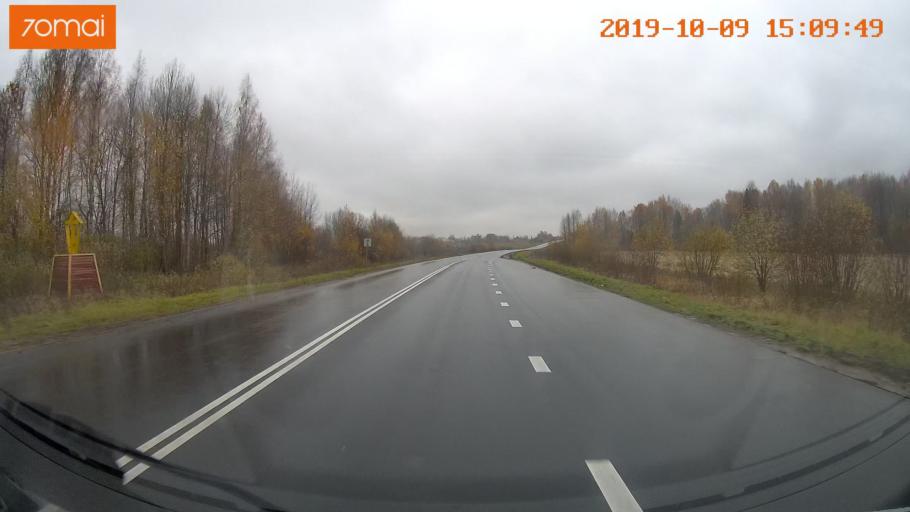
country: RU
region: Kostroma
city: Susanino
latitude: 58.1862
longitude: 41.6483
